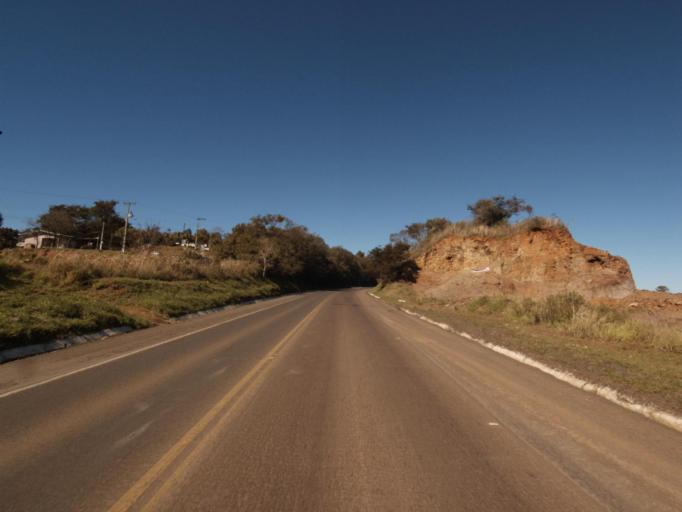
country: BR
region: Santa Catarina
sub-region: Sao Lourenco Do Oeste
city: Sao Lourenco dOeste
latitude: -26.7867
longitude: -53.1953
